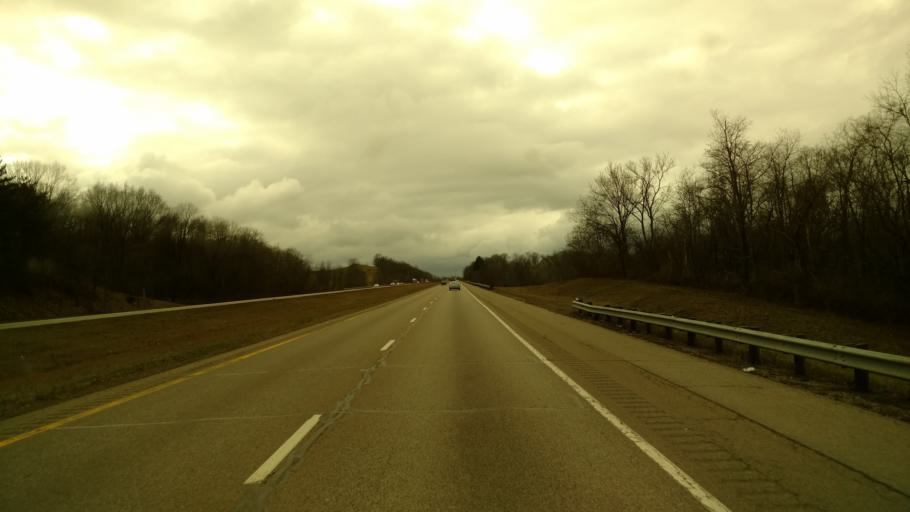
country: US
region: Ohio
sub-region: Muskingum County
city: Zanesville
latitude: 39.9463
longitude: -82.0718
